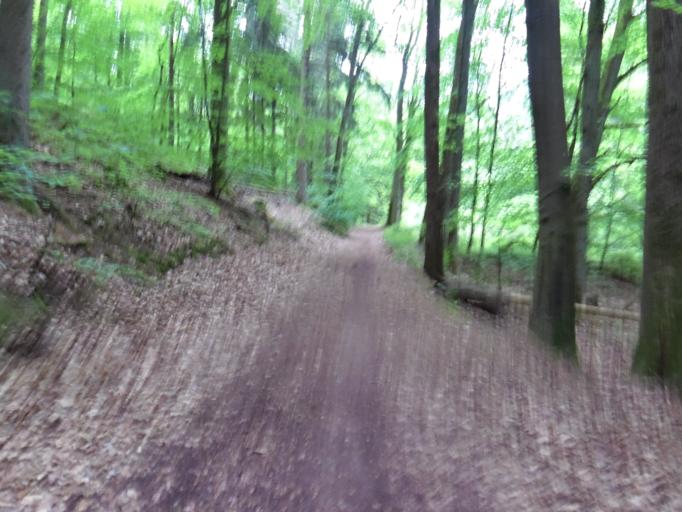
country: DE
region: Rheinland-Pfalz
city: Bad Duerkheim
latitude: 49.4390
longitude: 8.1185
